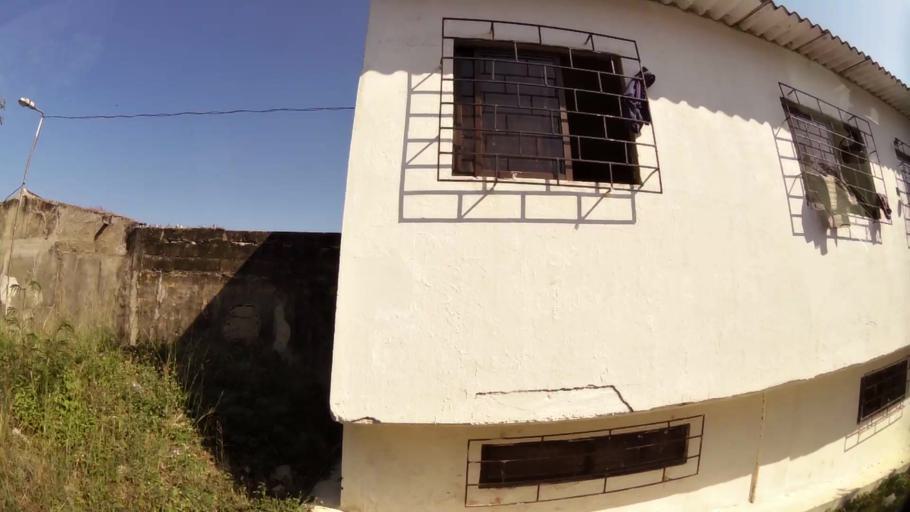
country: CO
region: Bolivar
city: Cartagena
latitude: 10.3689
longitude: -75.5038
